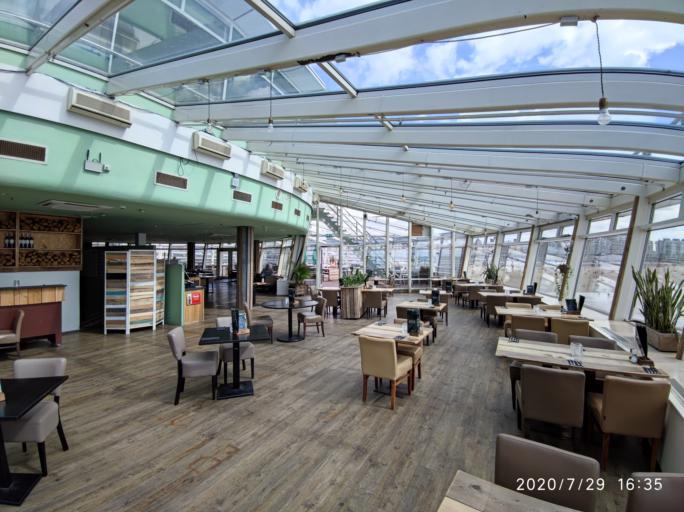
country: NL
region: South Holland
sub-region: Gemeente Den Haag
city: Scheveningen
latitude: 52.1170
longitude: 4.2796
